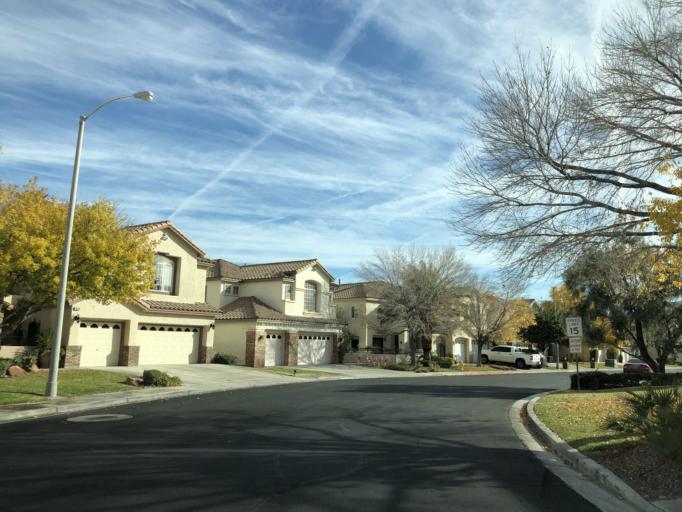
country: US
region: Nevada
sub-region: Clark County
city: Whitney
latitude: 36.0198
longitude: -115.0712
